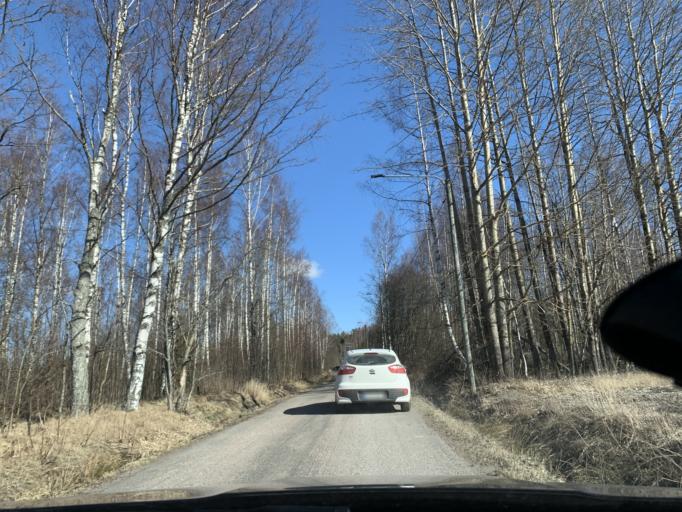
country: FI
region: Uusimaa
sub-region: Helsinki
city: Espoo
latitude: 60.1756
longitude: 24.5852
